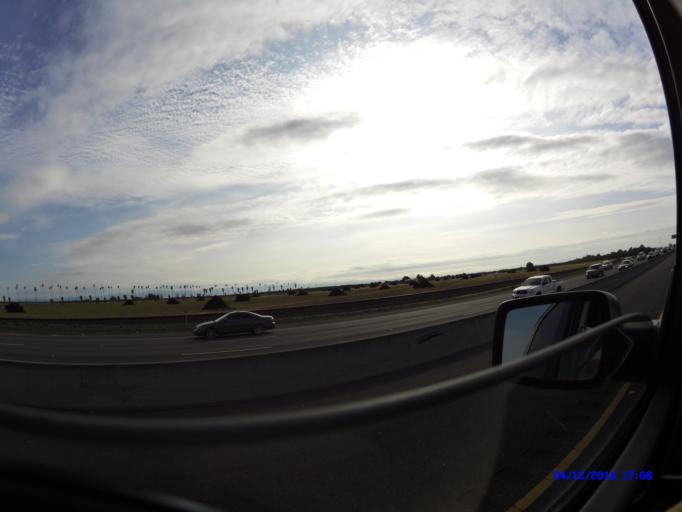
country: US
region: California
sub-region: San Joaquin County
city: Ripon
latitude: 37.7684
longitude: -121.1701
